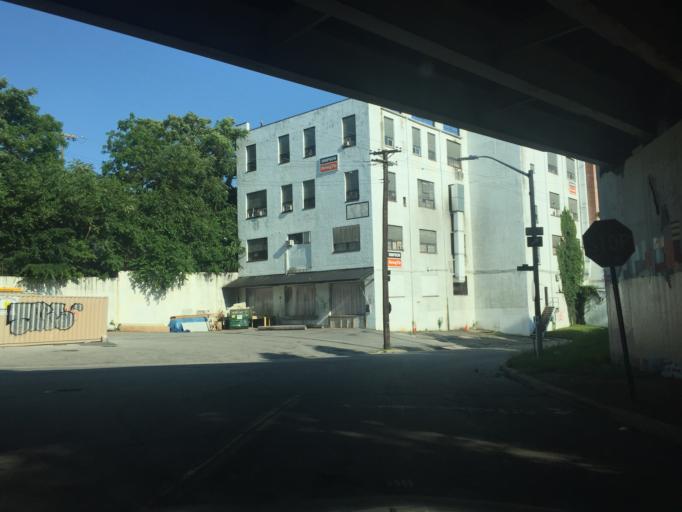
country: US
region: Maryland
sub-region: City of Baltimore
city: Baltimore
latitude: 39.3271
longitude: -76.6328
